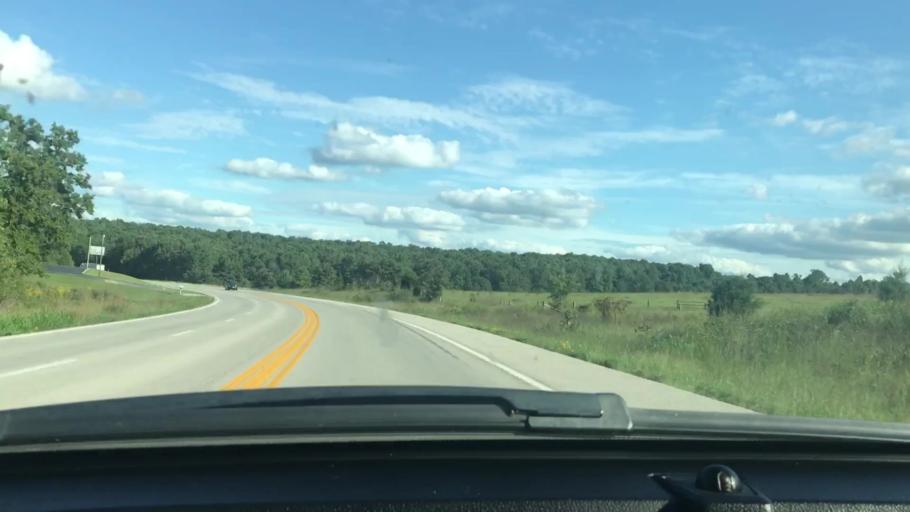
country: US
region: Missouri
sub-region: Howell County
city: West Plains
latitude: 36.6619
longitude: -91.7215
